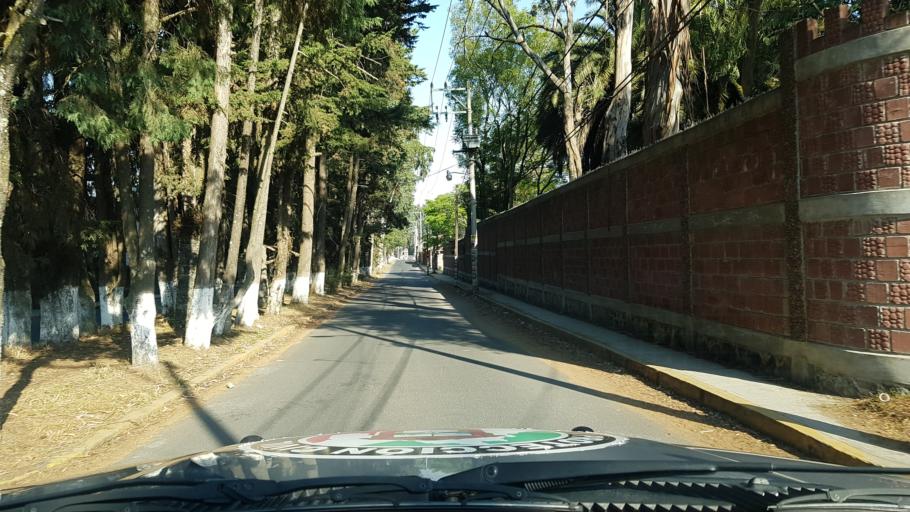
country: MX
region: Mexico
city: Ozumba de Alzate
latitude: 19.0622
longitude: -98.7826
